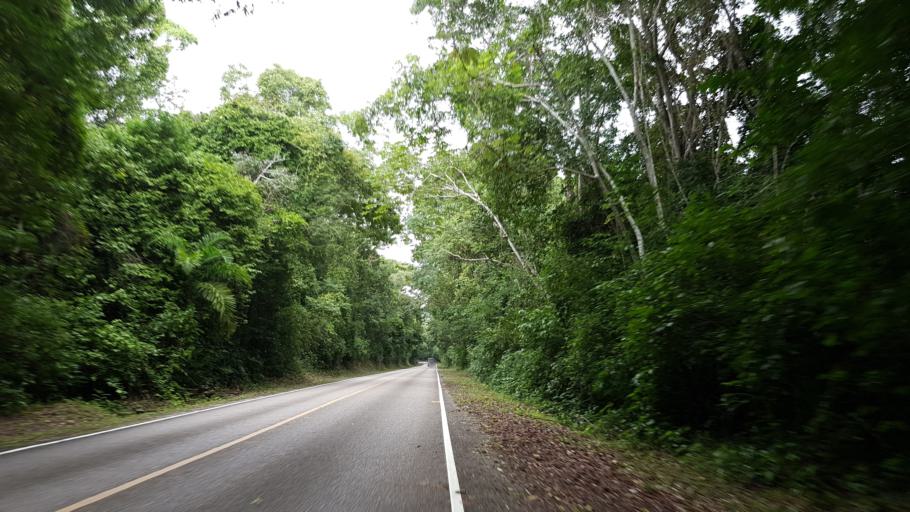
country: GT
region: Peten
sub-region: Municipio de San Jose
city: San Jose
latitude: 17.2114
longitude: -89.6148
